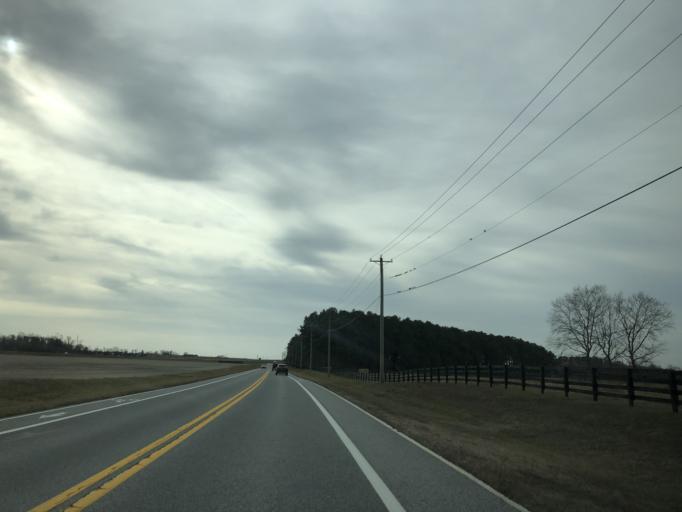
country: US
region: Delaware
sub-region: New Castle County
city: Middletown
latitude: 39.4722
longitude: -75.7384
